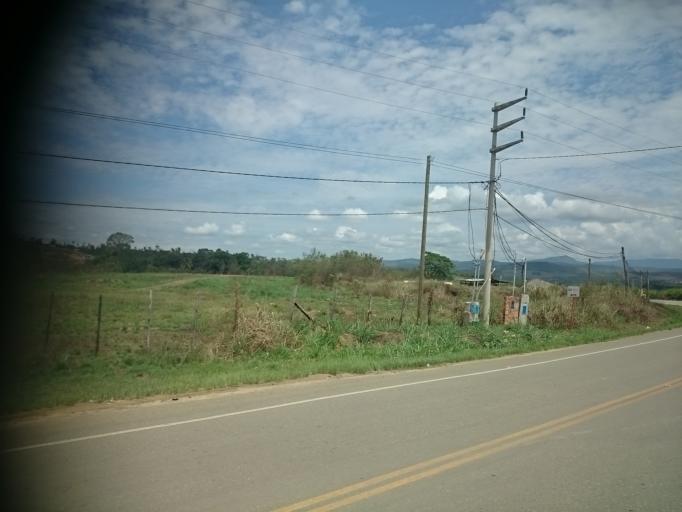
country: PE
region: San Martin
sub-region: Provincia de San Martin
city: Tarapoto
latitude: -6.5101
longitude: -76.3551
